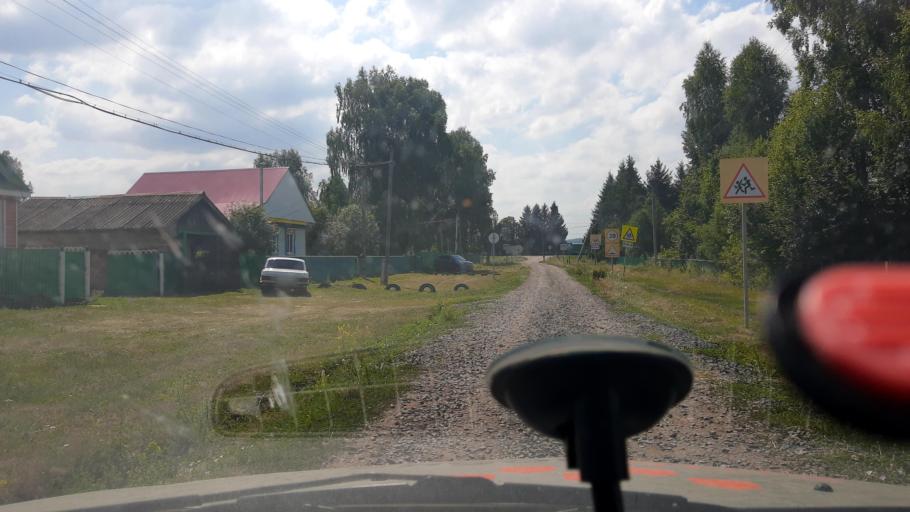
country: RU
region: Bashkortostan
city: Chekmagush
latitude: 54.8775
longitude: 54.6146
